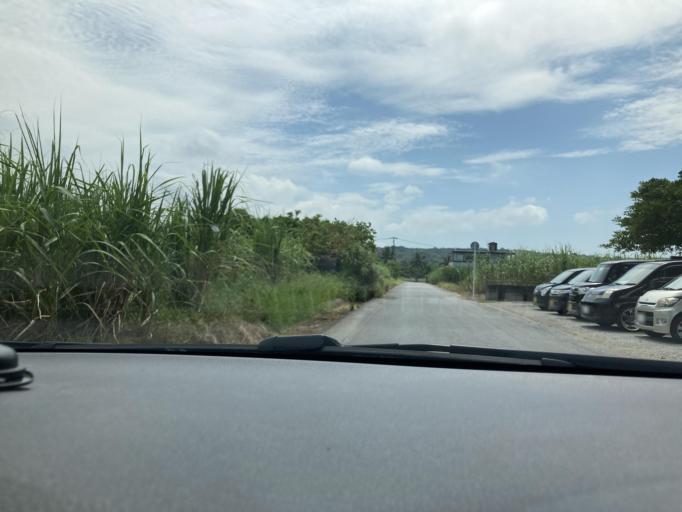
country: JP
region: Okinawa
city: Ishikawa
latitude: 26.4404
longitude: 127.7730
